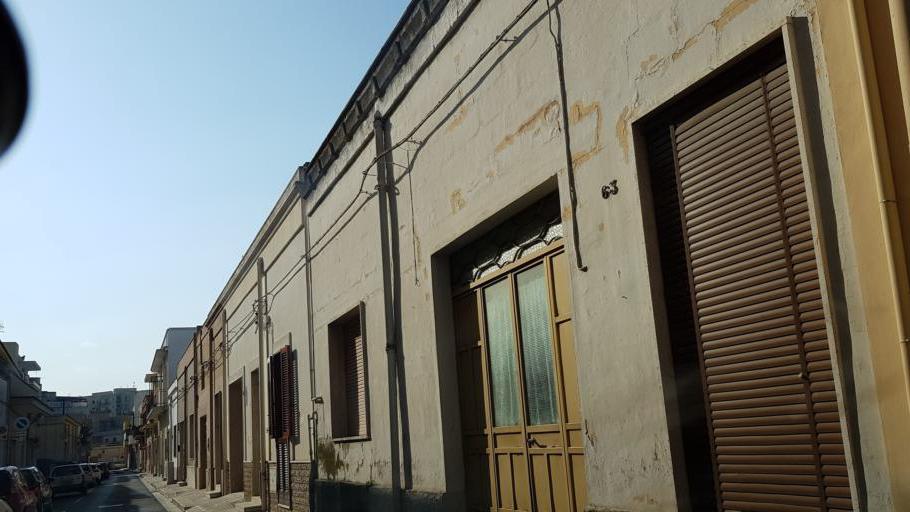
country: IT
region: Apulia
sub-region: Provincia di Brindisi
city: Mesagne
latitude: 40.5635
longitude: 17.8072
